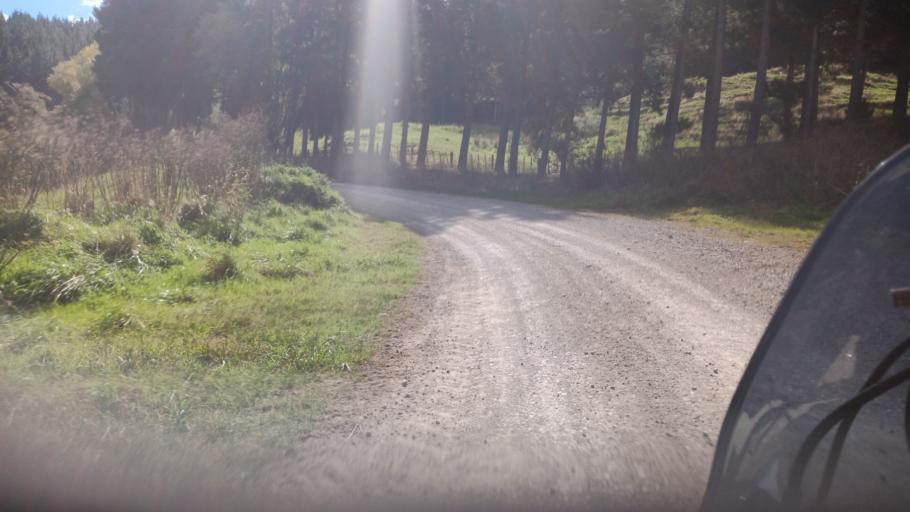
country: NZ
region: Gisborne
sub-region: Gisborne District
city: Gisborne
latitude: -38.4011
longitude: 177.6806
